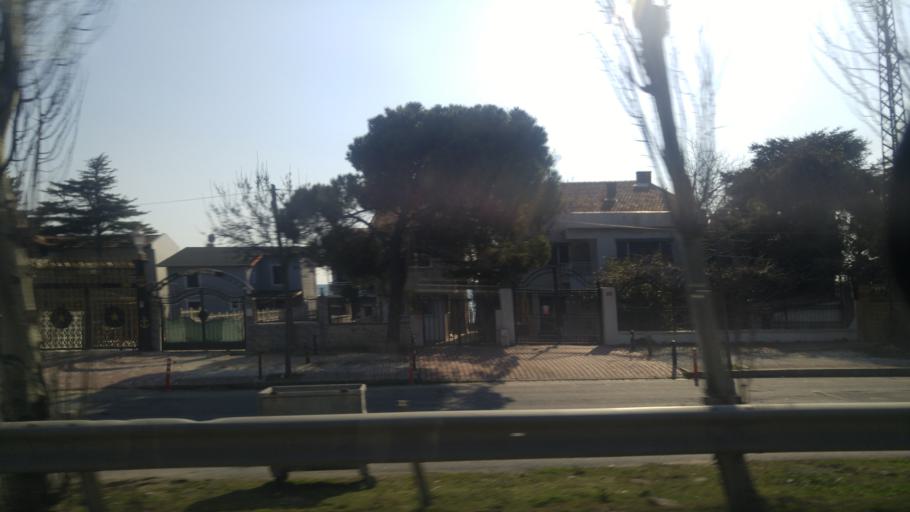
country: TR
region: Istanbul
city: Celaliye
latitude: 41.0417
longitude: 28.4219
